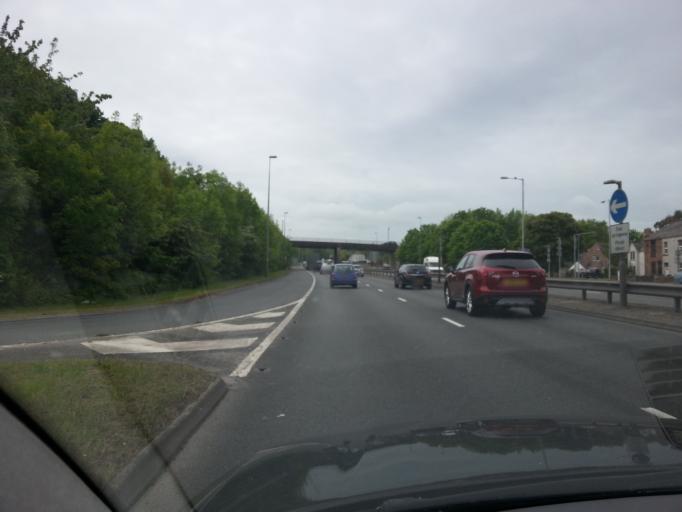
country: GB
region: Wales
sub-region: County of Flintshire
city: Queensferry
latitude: 53.2006
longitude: -3.0357
